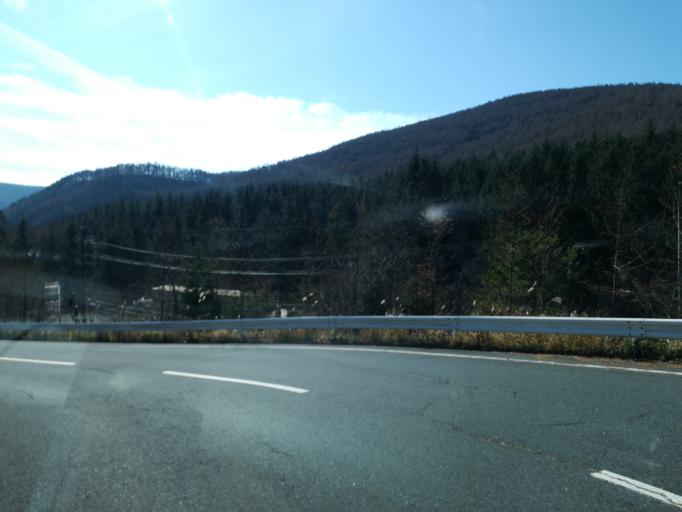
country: JP
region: Nagano
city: Ueda
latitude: 36.5190
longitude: 138.3396
